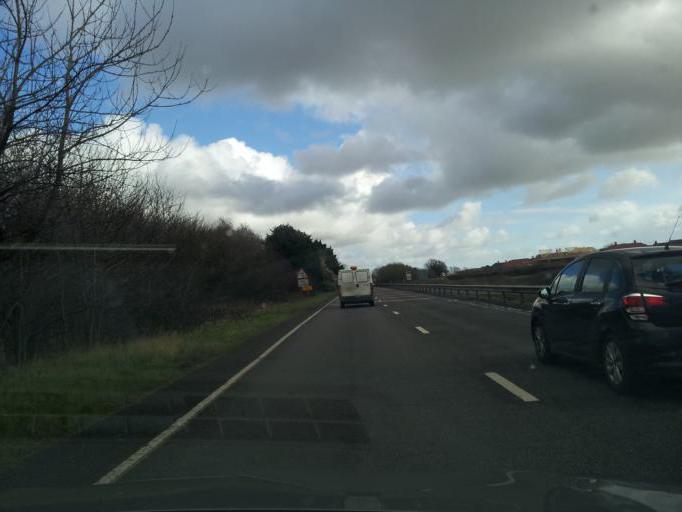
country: GB
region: England
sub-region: Norfolk
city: Brundall
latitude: 52.6314
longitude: 1.4184
